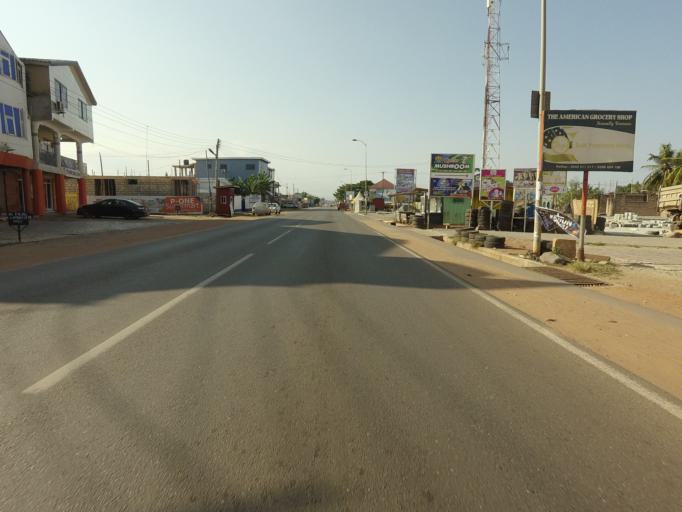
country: GH
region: Greater Accra
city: Nungua
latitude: 5.6326
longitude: -0.0762
